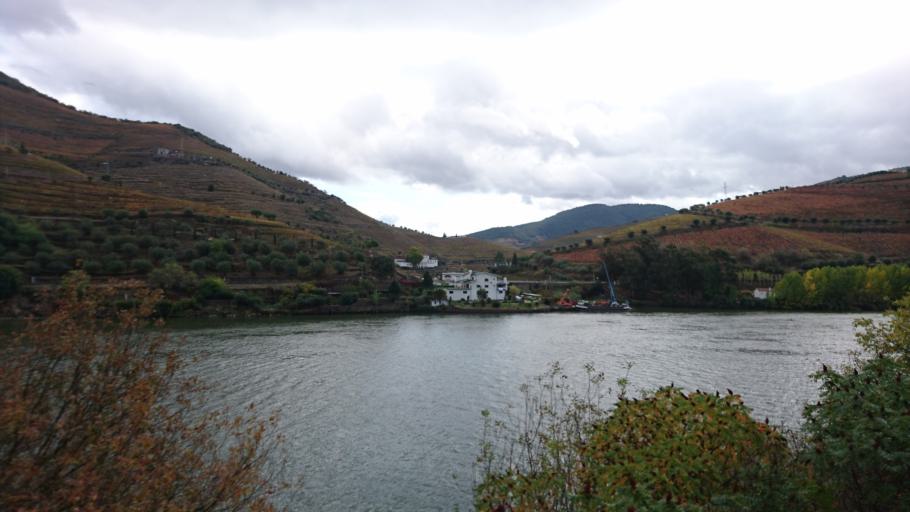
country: PT
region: Viseu
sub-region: Tabuaco
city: Tabuaco
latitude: 41.1764
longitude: -7.5556
